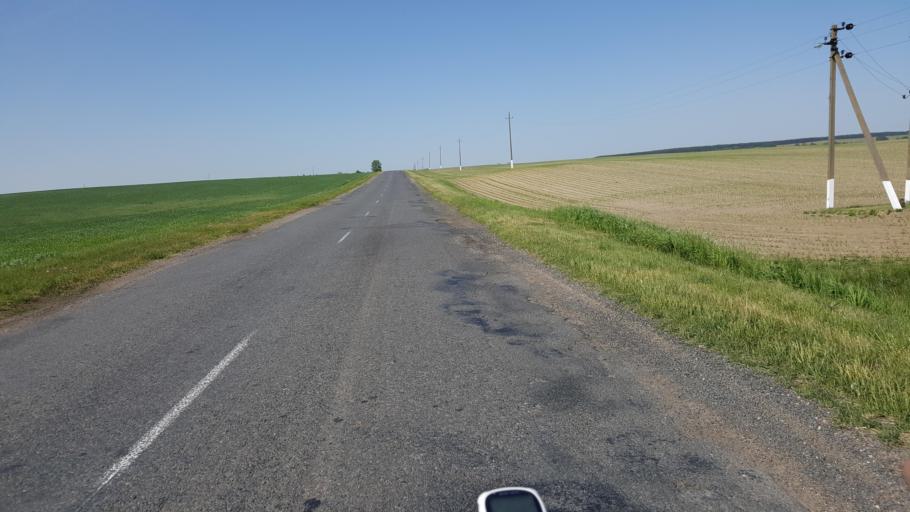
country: BY
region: Brest
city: Charnawchytsy
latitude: 52.2916
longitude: 23.6055
